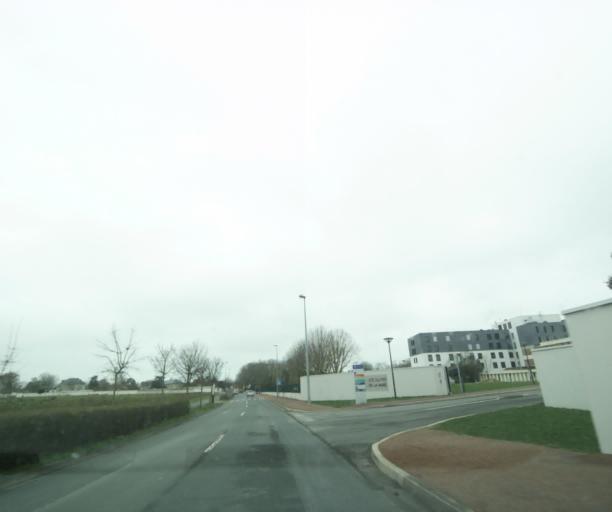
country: FR
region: Poitou-Charentes
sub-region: Departement de la Charente-Maritime
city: Puilboreau
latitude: 46.1746
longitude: -1.1298
